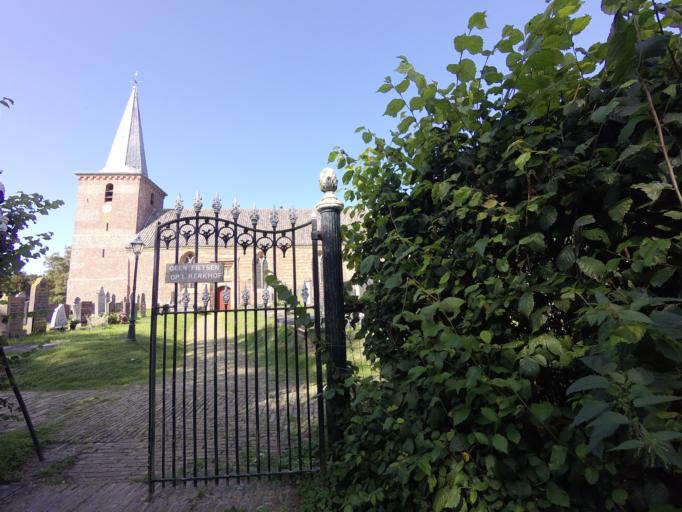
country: NL
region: Friesland
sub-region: Gemeente Terschelling
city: West-Terschelling
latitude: 53.3970
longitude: 5.3418
